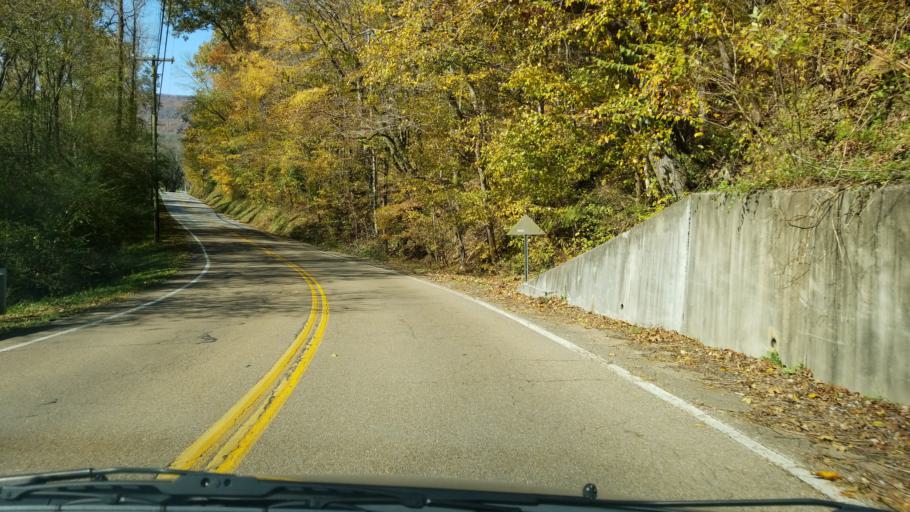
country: US
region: Tennessee
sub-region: Hamilton County
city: Falling Water
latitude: 35.1987
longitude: -85.2478
